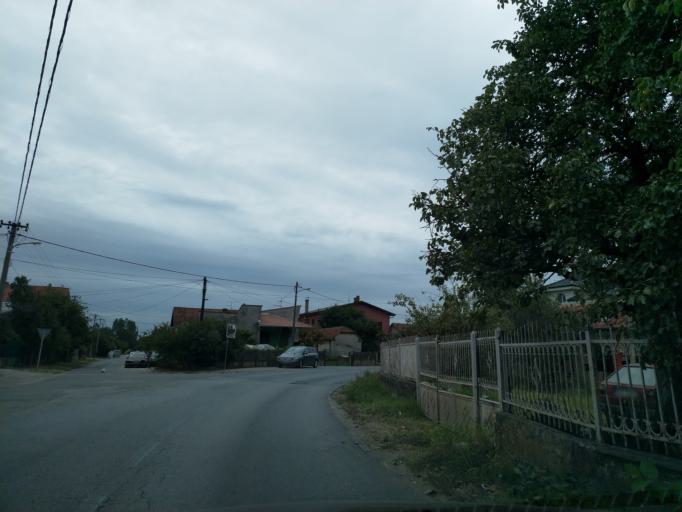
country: RS
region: Central Serbia
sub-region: Pomoravski Okrug
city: Paracin
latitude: 43.8550
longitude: 21.3973
